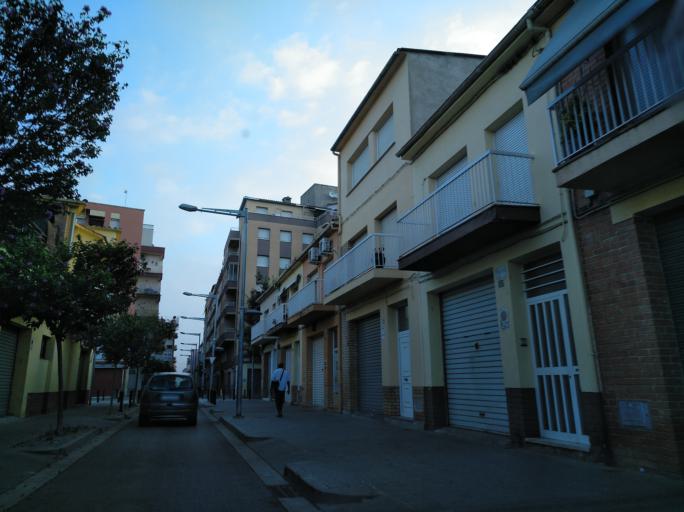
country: ES
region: Catalonia
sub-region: Provincia de Girona
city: Salt
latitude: 41.9725
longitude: 2.7884
